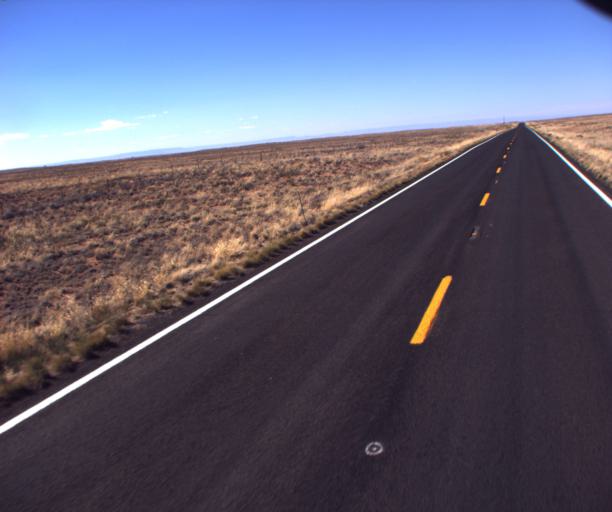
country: US
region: Arizona
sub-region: Coconino County
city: Tuba City
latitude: 35.9757
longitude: -110.9755
